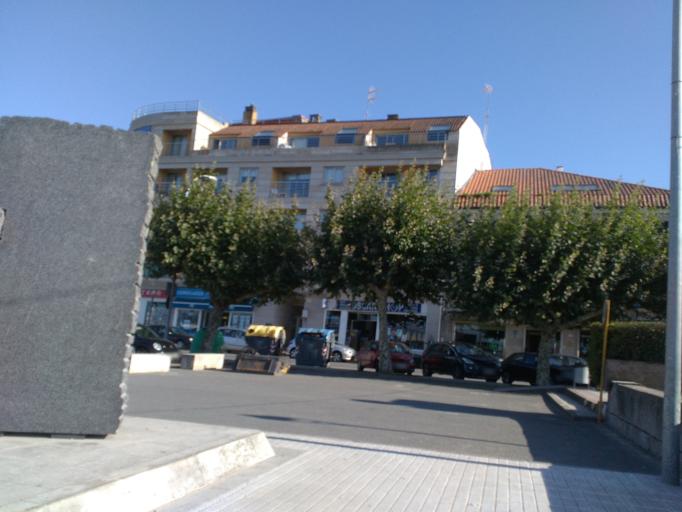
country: ES
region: Galicia
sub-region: Provincia de Pontevedra
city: Bueu
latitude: 42.3270
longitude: -8.7872
